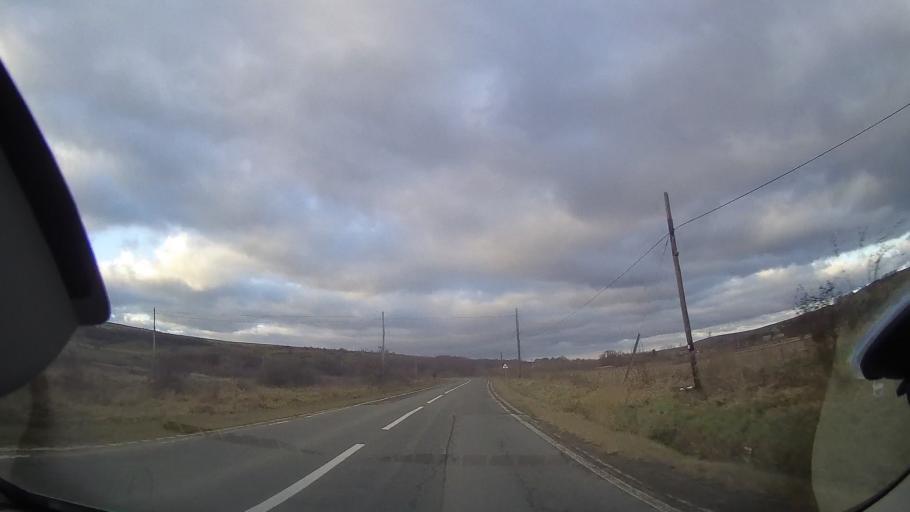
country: RO
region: Cluj
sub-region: Comuna Calatele
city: Calatele
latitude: 46.7932
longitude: 22.9965
